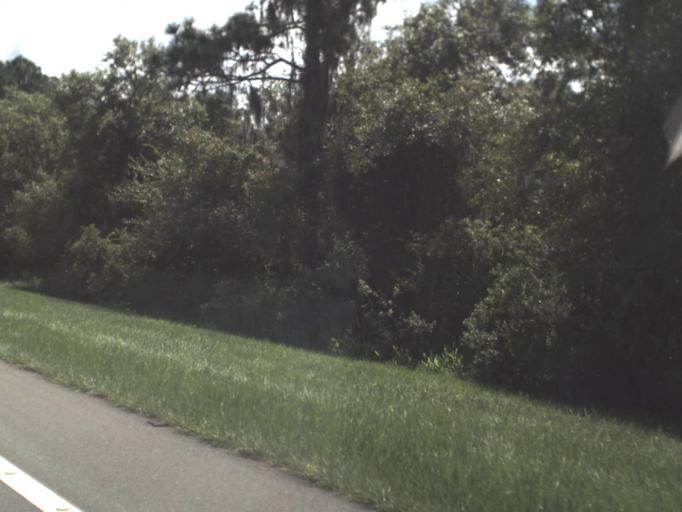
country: US
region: Florida
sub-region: Sarasota County
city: The Meadows
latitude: 27.4167
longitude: -82.3561
